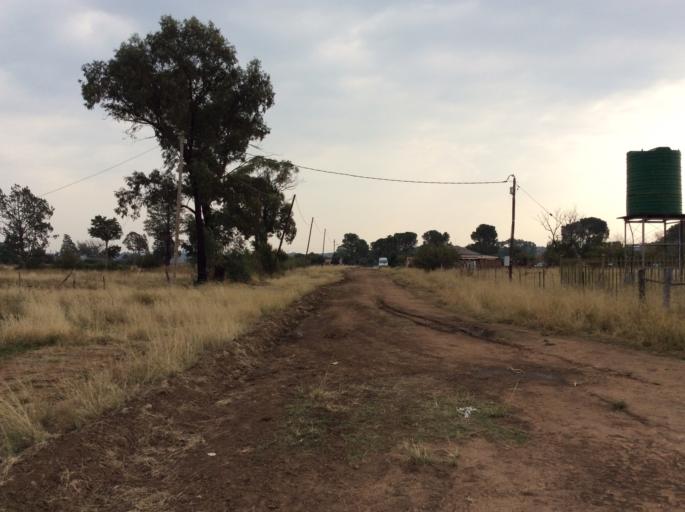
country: LS
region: Mafeteng
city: Mafeteng
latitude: -29.9907
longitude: 27.0173
